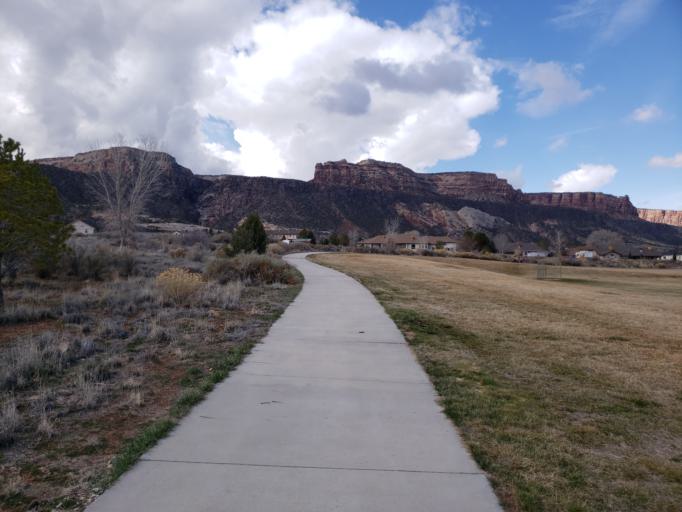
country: US
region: Colorado
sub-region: Mesa County
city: Redlands
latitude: 39.0559
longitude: -108.6462
